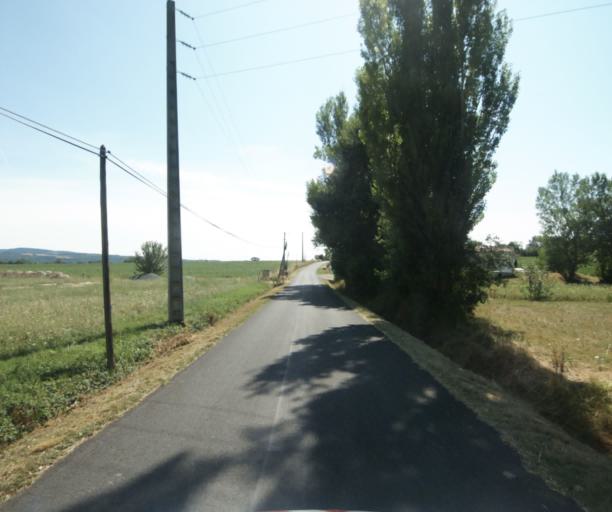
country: FR
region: Midi-Pyrenees
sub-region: Departement de la Haute-Garonne
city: Revel
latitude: 43.4847
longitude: 2.0129
